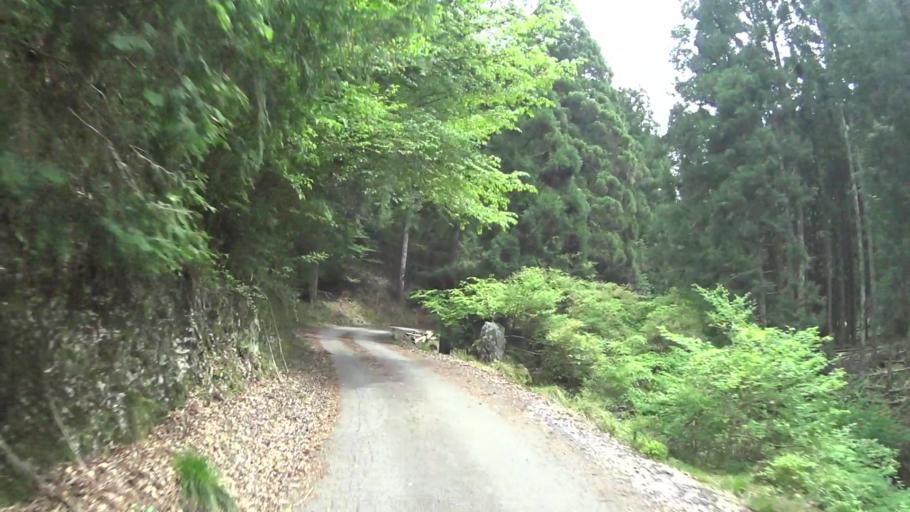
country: JP
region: Kyoto
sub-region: Kyoto-shi
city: Kamigyo-ku
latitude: 35.1890
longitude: 135.7035
